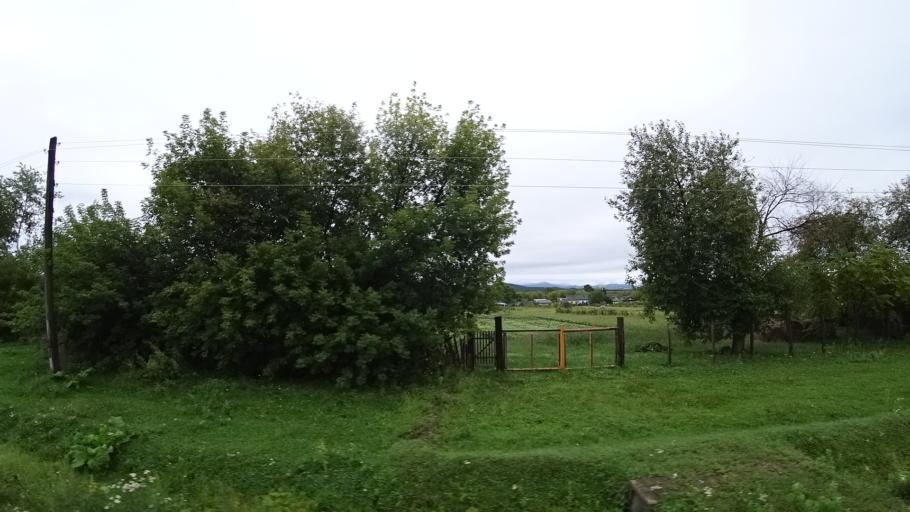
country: RU
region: Primorskiy
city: Monastyrishche
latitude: 44.2582
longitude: 132.4231
